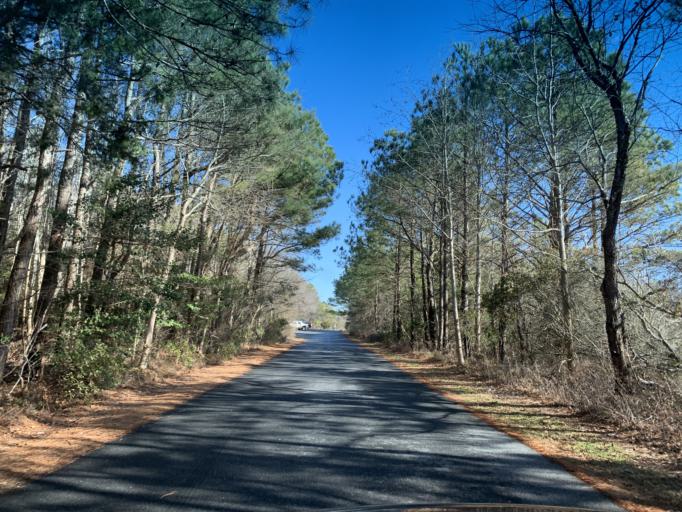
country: US
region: Maryland
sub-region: Worcester County
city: Ocean Pines
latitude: 38.3892
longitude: -75.1062
